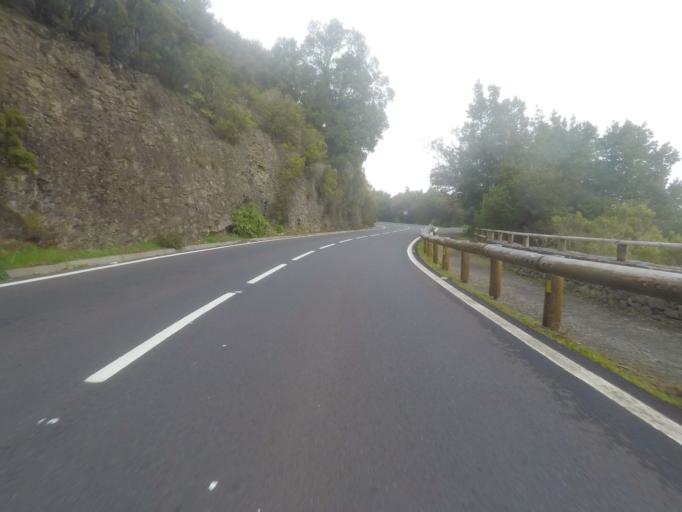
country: ES
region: Canary Islands
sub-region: Provincia de Santa Cruz de Tenerife
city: Alajero
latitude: 28.1131
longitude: -17.2420
